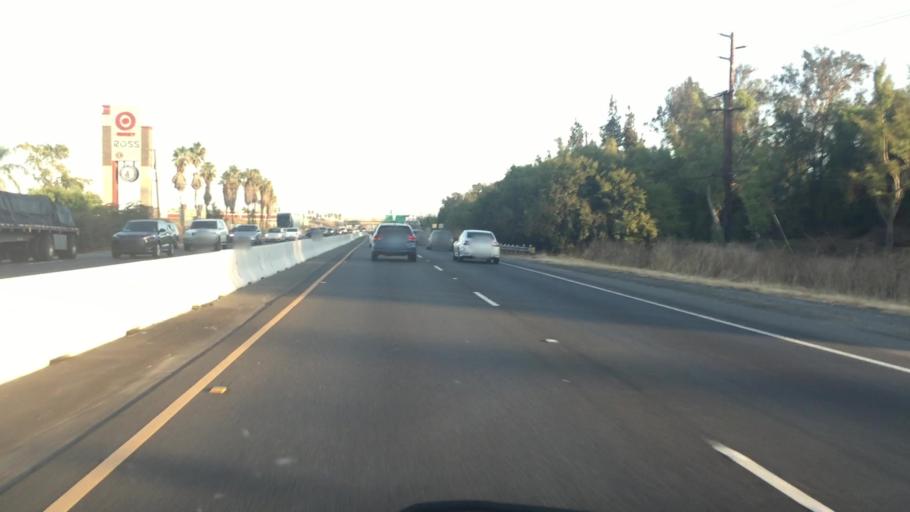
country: US
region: California
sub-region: Los Angeles County
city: Pomona
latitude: 34.0371
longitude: -117.7639
